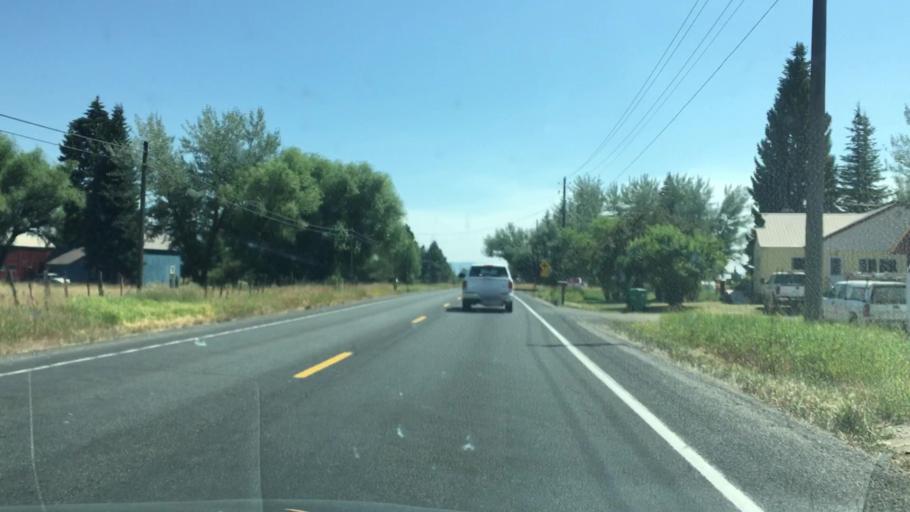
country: US
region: Idaho
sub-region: Valley County
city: McCall
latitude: 44.8497
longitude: -116.0905
